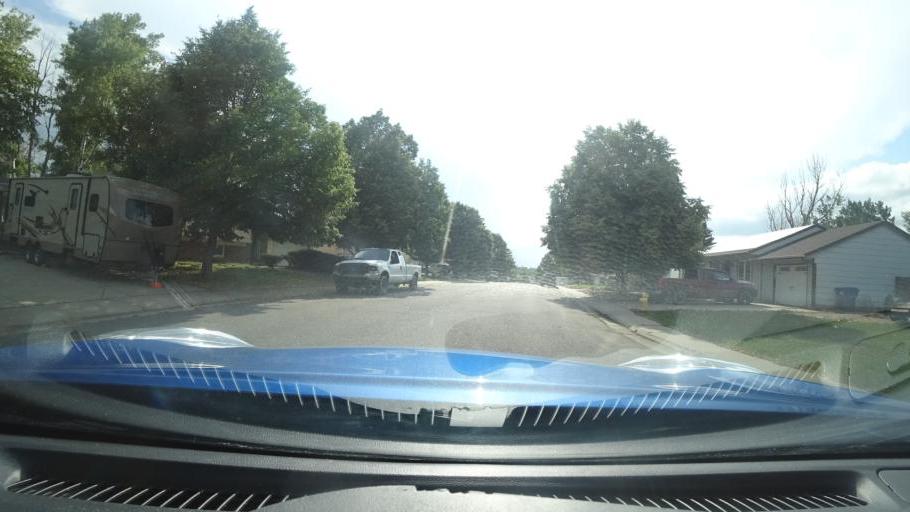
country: US
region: Colorado
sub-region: Adams County
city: Aurora
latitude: 39.6897
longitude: -104.7973
